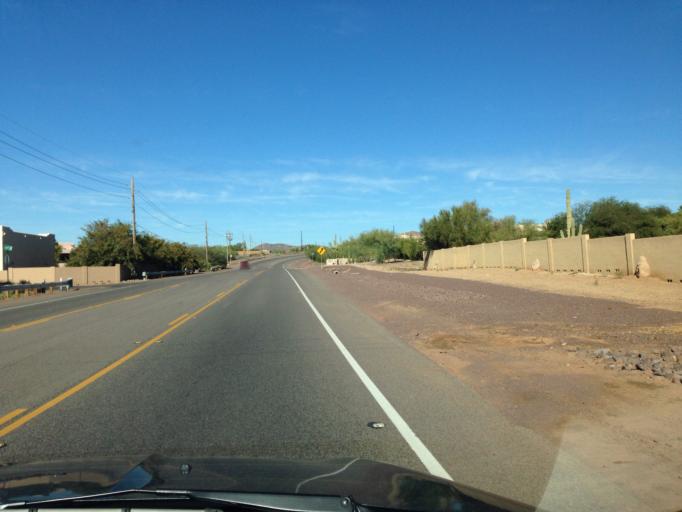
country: US
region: Arizona
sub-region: Maricopa County
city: Anthem
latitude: 33.8383
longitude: -112.0654
